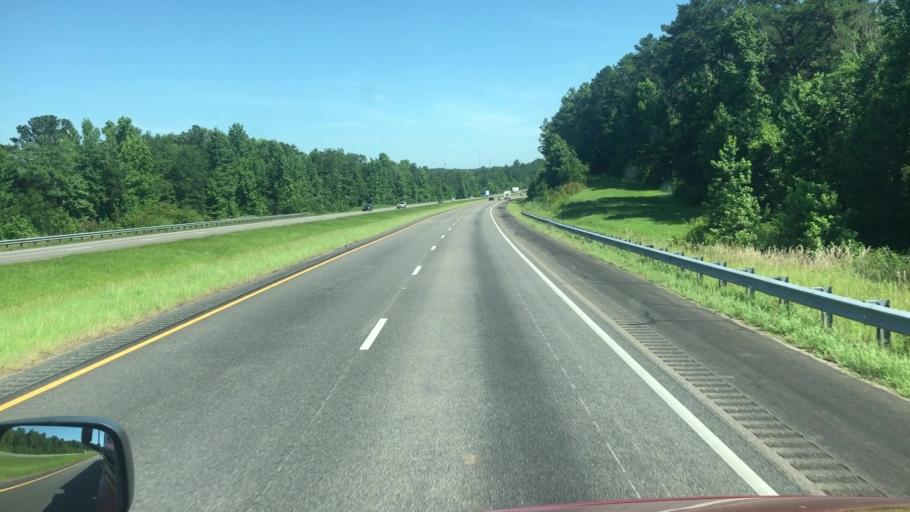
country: US
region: Alabama
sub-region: Autauga County
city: Pine Level
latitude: 32.5909
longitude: -86.4754
